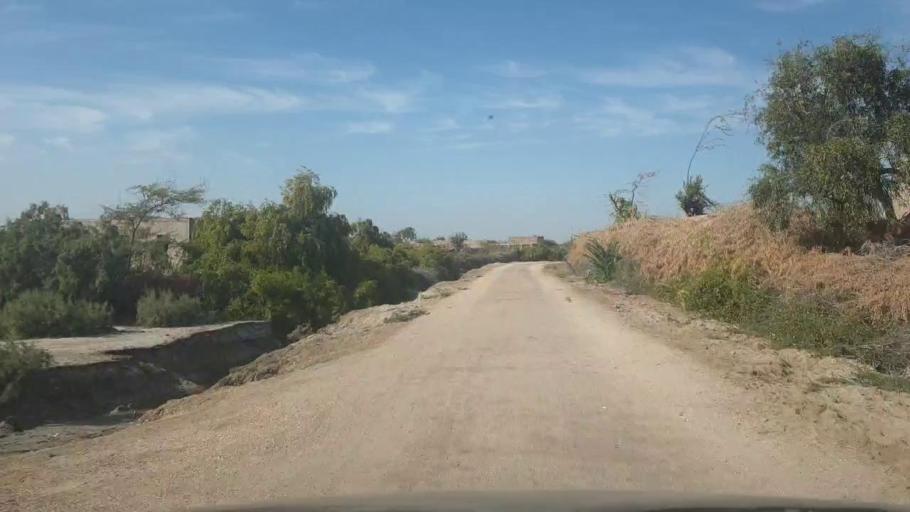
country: PK
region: Sindh
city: Pithoro
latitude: 25.3960
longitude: 69.2517
